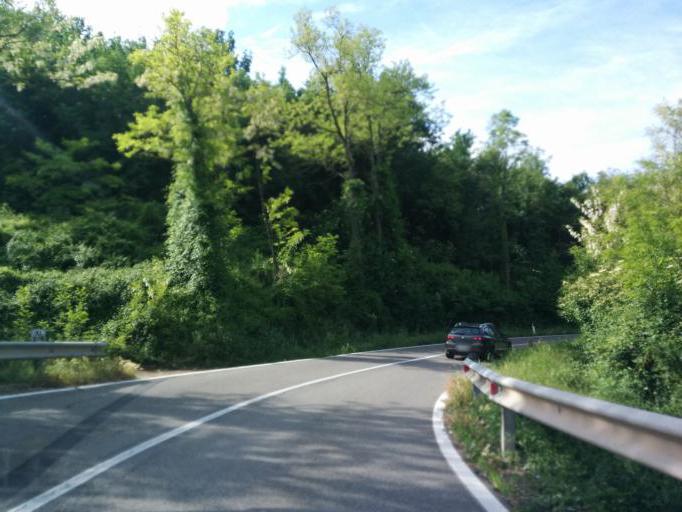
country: IT
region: Tuscany
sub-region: Province of Florence
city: San Casciano in Val di Pesa
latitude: 43.6408
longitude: 11.1767
